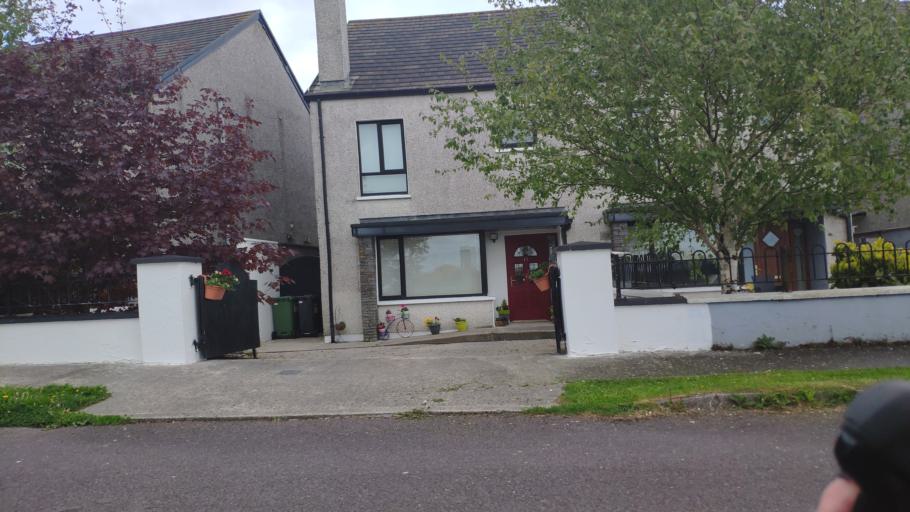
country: IE
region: Munster
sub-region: County Cork
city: Cork
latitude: 51.9110
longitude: -8.5059
